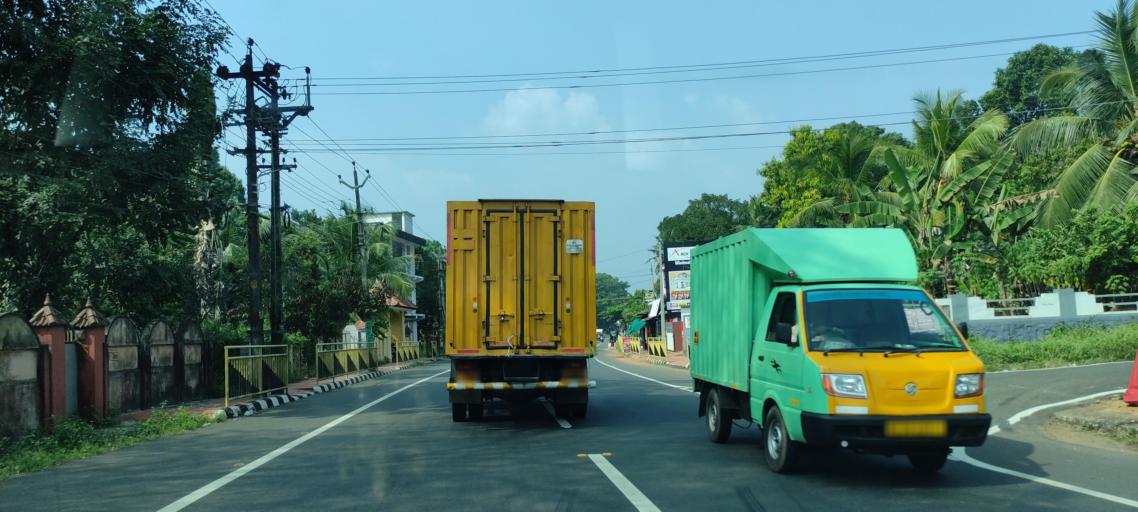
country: IN
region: Kerala
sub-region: Alappuzha
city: Chengannur
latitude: 9.2700
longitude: 76.6556
